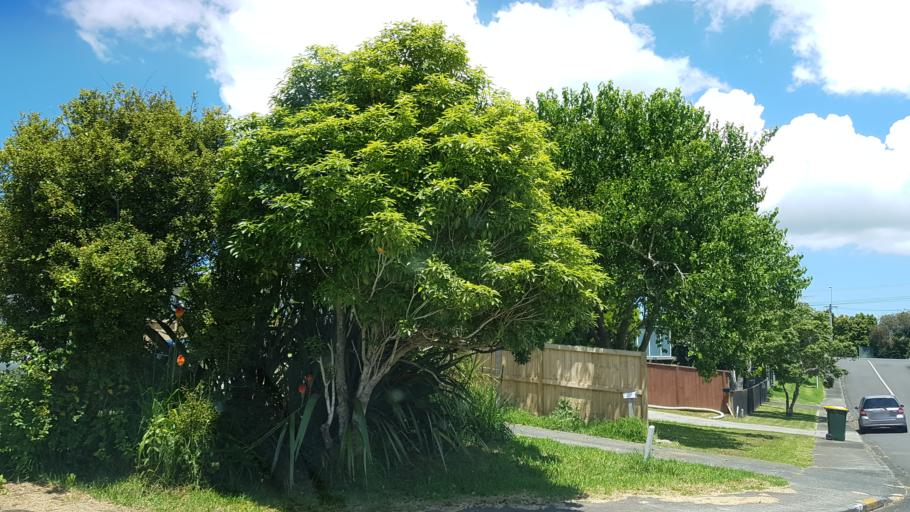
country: NZ
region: Auckland
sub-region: Auckland
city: North Shore
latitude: -36.7950
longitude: 174.6905
